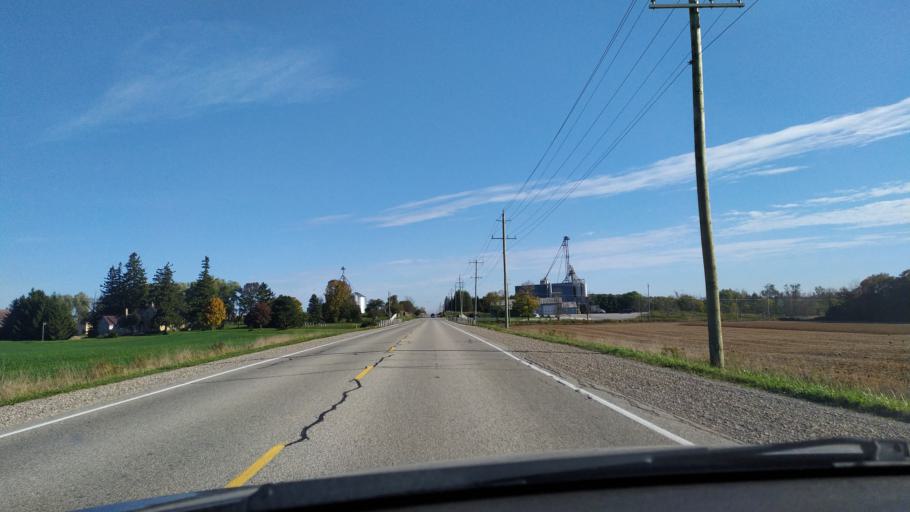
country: CA
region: Ontario
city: Stratford
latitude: 43.4947
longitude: -80.7687
